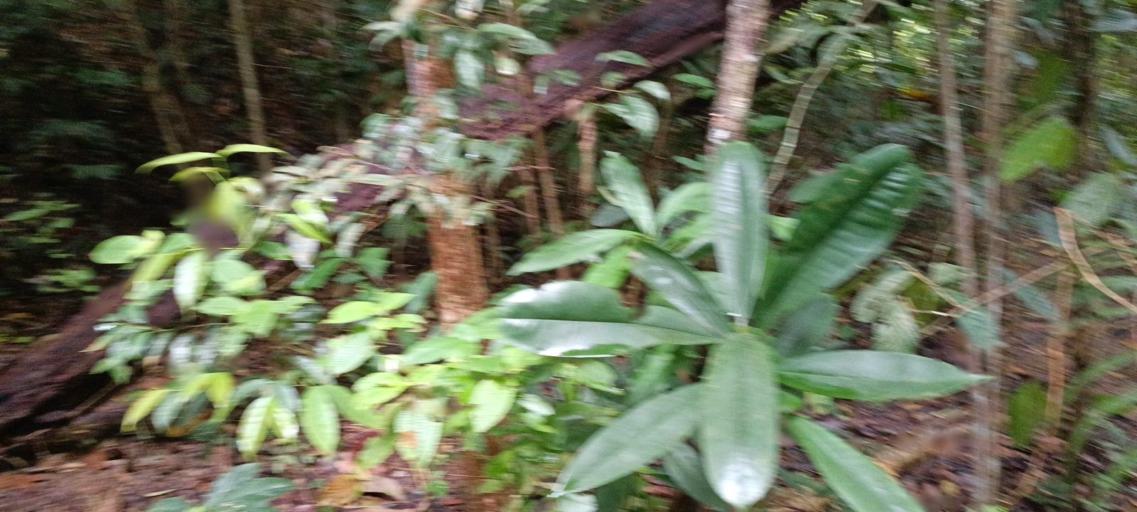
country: MY
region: Penang
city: Bukit Mertajam
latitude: 5.3614
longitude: 100.4884
